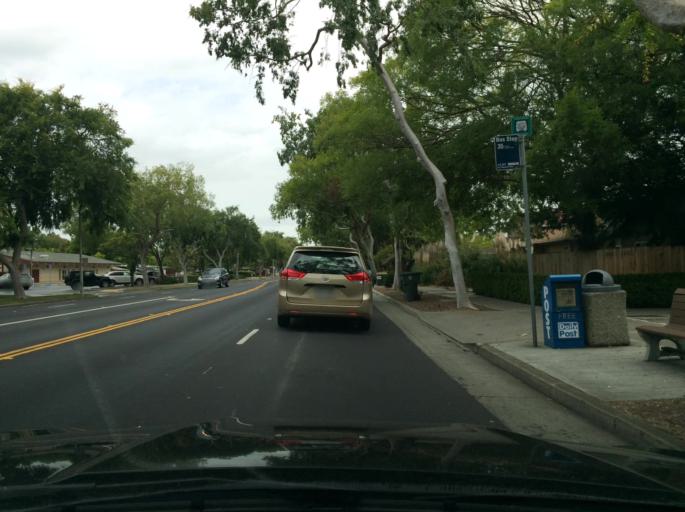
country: US
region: California
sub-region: Santa Clara County
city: Los Altos
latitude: 37.4202
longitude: -122.1102
